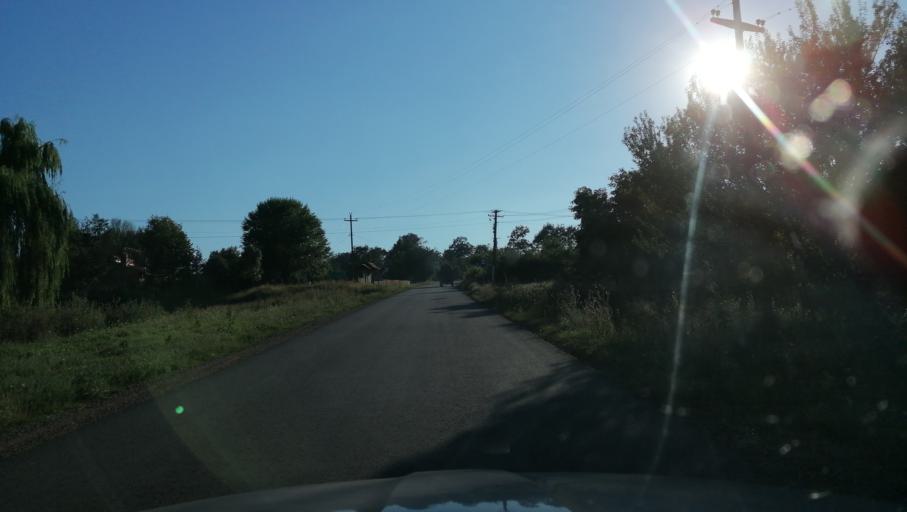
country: RS
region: Central Serbia
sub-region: Sumadijski Okrug
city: Kragujevac
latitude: 44.1078
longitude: 20.8266
